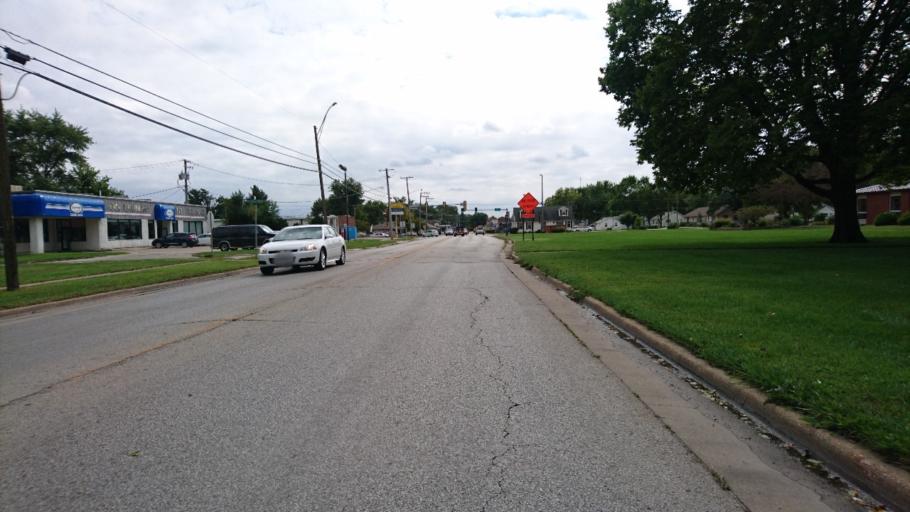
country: US
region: Illinois
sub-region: Livingston County
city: Pontiac
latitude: 40.8822
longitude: -88.6381
